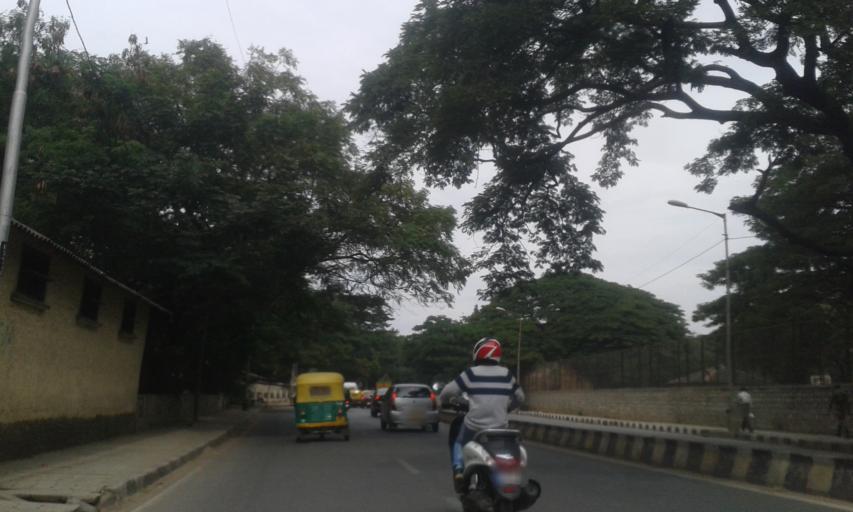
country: IN
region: Karnataka
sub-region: Bangalore Urban
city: Bangalore
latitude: 12.9639
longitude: 77.6183
